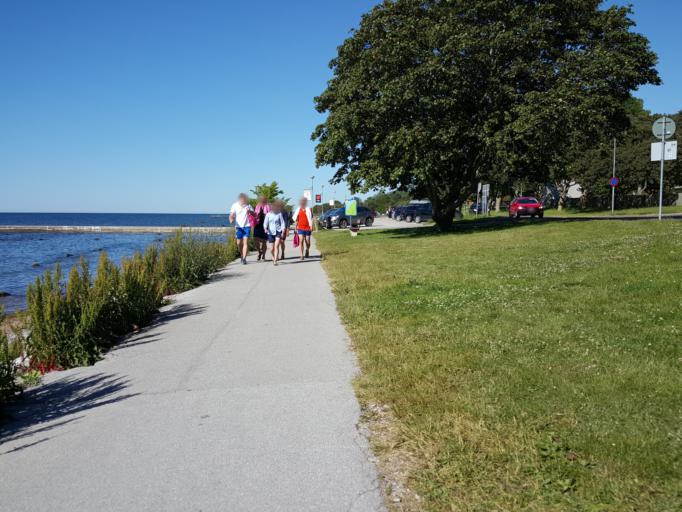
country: SE
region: Gotland
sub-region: Gotland
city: Visby
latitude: 57.6483
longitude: 18.2977
